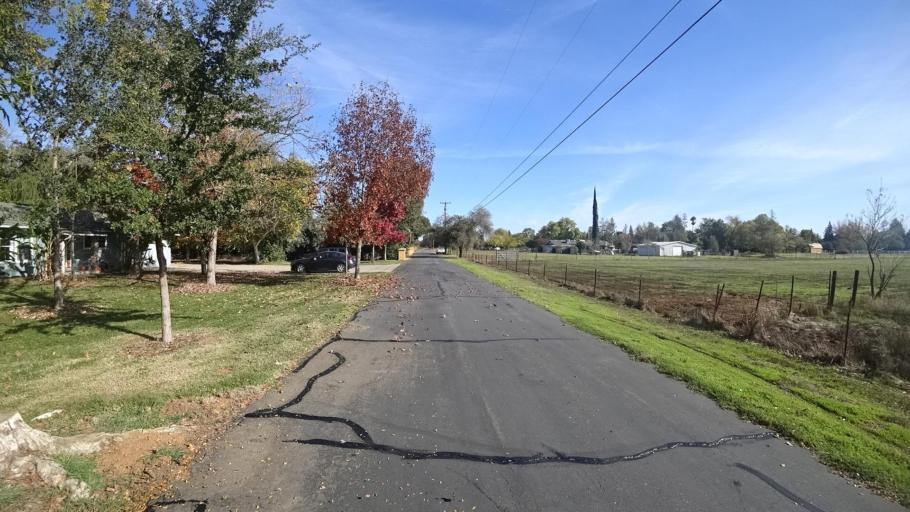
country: US
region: California
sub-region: Sacramento County
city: Vineyard
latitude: 38.4437
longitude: -121.3136
